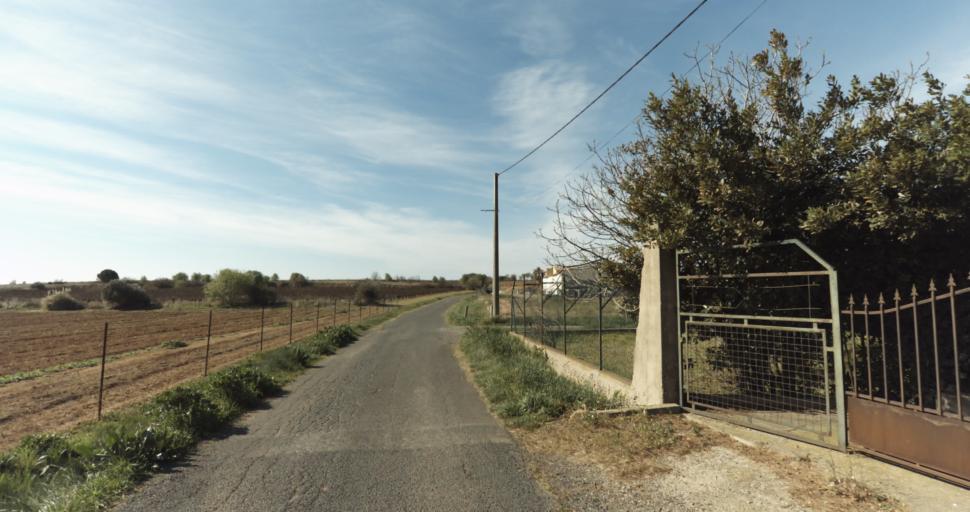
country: FR
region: Languedoc-Roussillon
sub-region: Departement de l'Herault
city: Marseillan
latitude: 43.3481
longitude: 3.5242
